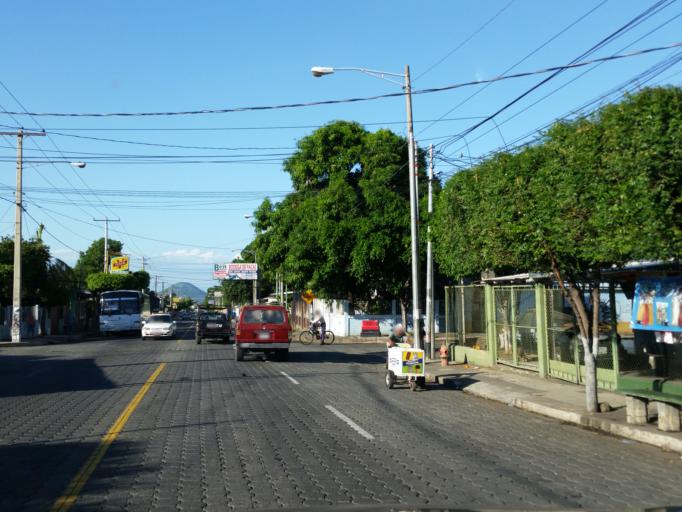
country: NI
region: Managua
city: Ciudad Sandino
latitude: 12.1467
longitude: -86.2975
